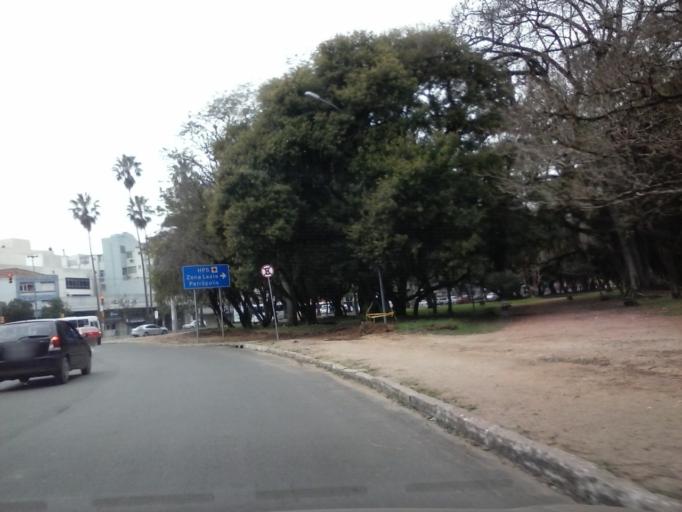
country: BR
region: Rio Grande do Sul
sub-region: Porto Alegre
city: Porto Alegre
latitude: -30.0345
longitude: -51.2191
